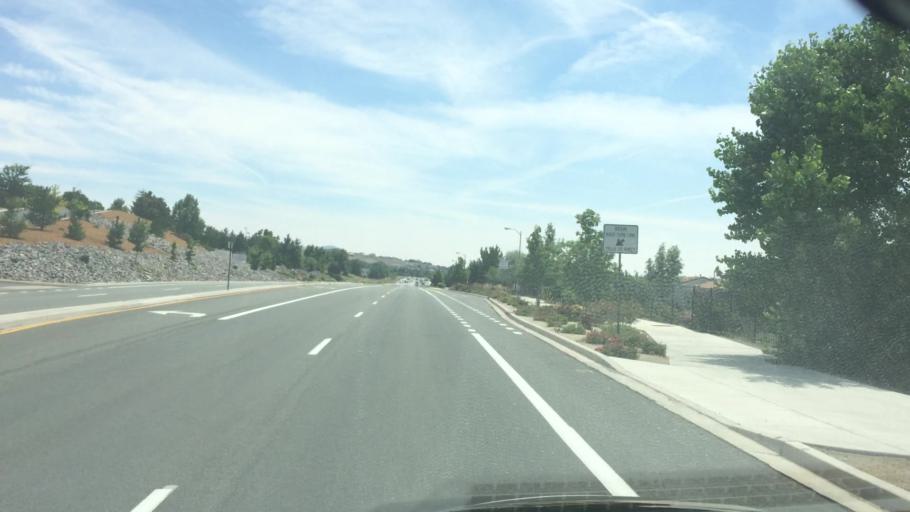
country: US
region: Nevada
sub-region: Washoe County
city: Spanish Springs
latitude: 39.5955
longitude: -119.7147
